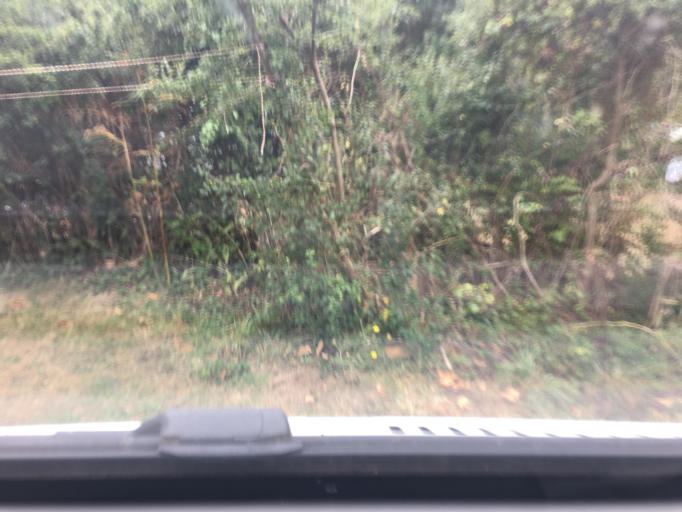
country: FR
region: Brittany
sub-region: Departement du Finistere
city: Beuzec-Cap-Sizun
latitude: 48.0830
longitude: -4.4816
